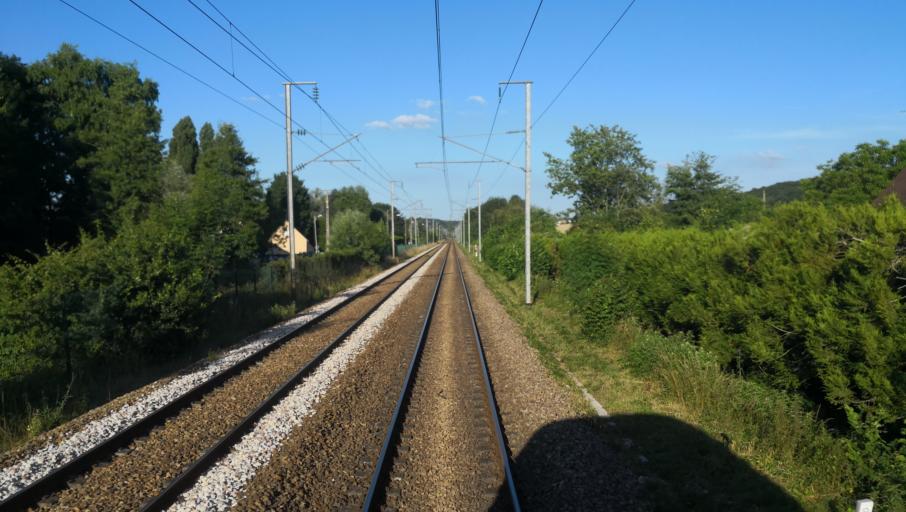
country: FR
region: Haute-Normandie
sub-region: Departement de l'Eure
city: Saint-Sebastien-de-Morsent
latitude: 48.9944
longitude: 1.0758
